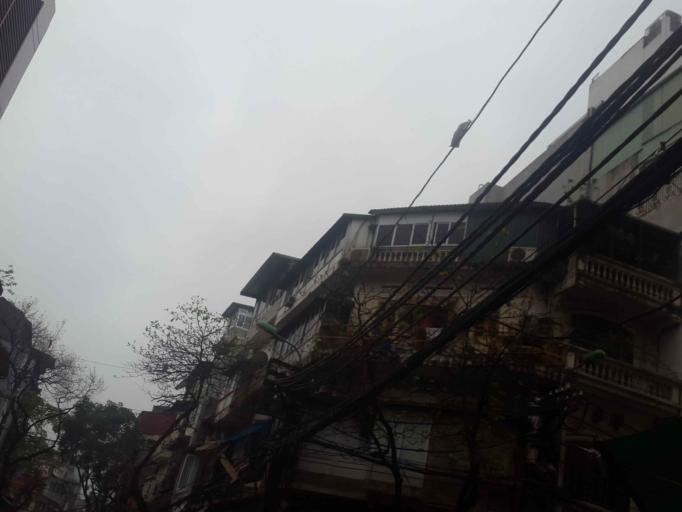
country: VN
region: Ha Noi
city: Hoan Kiem
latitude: 21.0333
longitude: 105.8502
